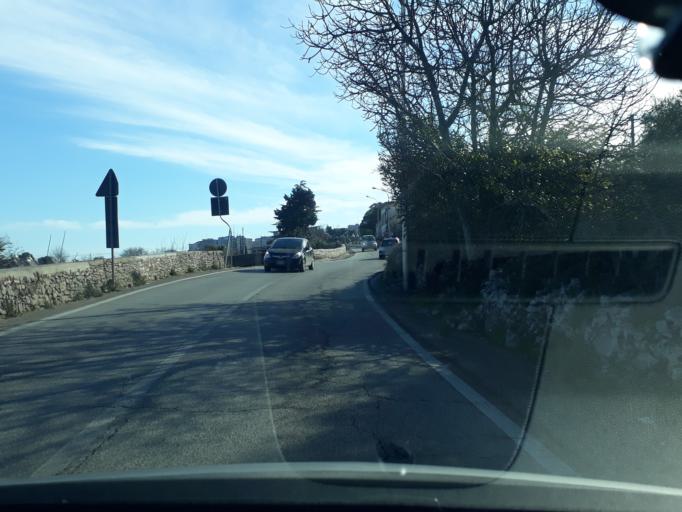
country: IT
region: Apulia
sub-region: Provincia di Taranto
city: Martina Franca
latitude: 40.7123
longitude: 17.3336
